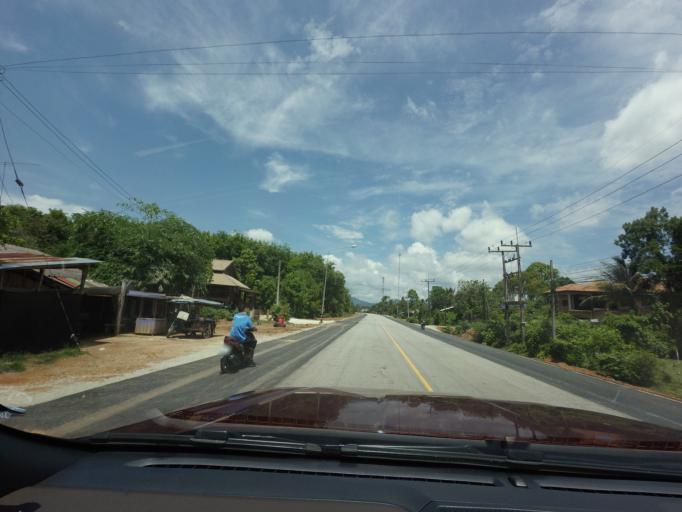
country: TH
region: Narathiwat
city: Ra-ngae
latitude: 6.2739
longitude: 101.6981
